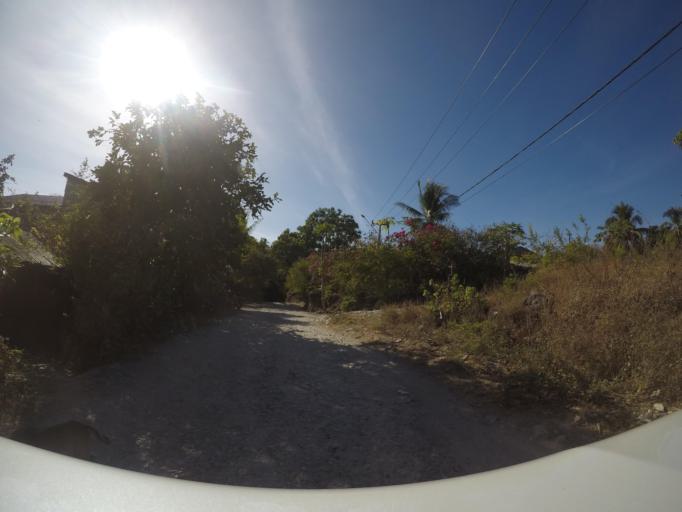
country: TL
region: Baucau
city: Baucau
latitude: -8.4567
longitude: 126.4443
